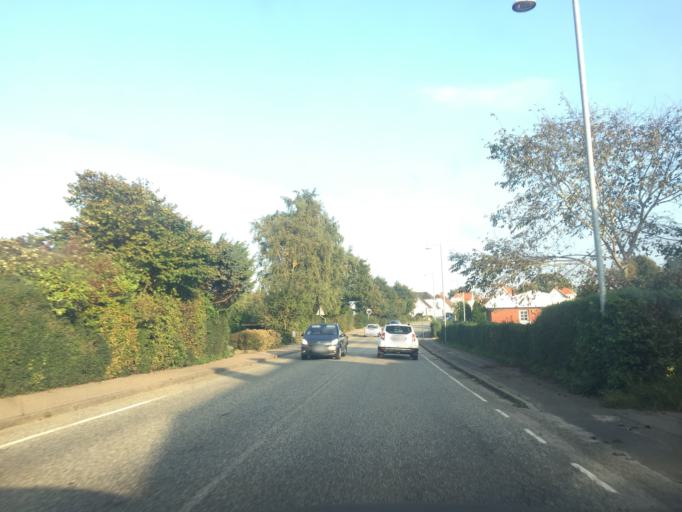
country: DK
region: Zealand
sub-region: Kalundborg Kommune
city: Hong
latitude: 55.5413
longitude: 11.3840
